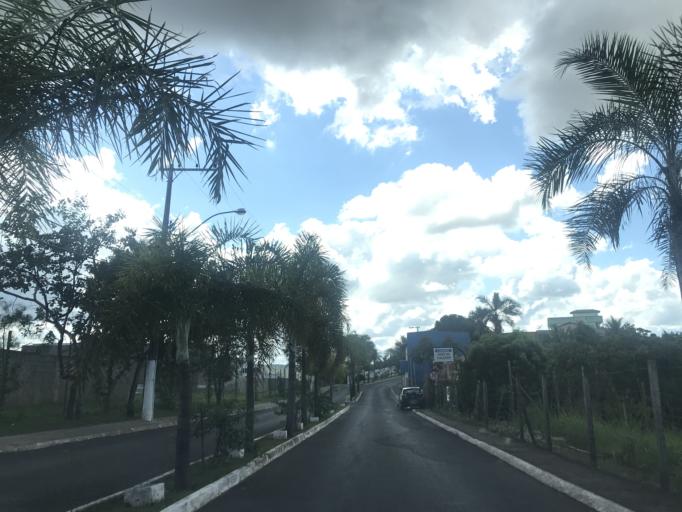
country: BR
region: Federal District
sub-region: Brasilia
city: Brasilia
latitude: -15.8695
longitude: -47.7602
